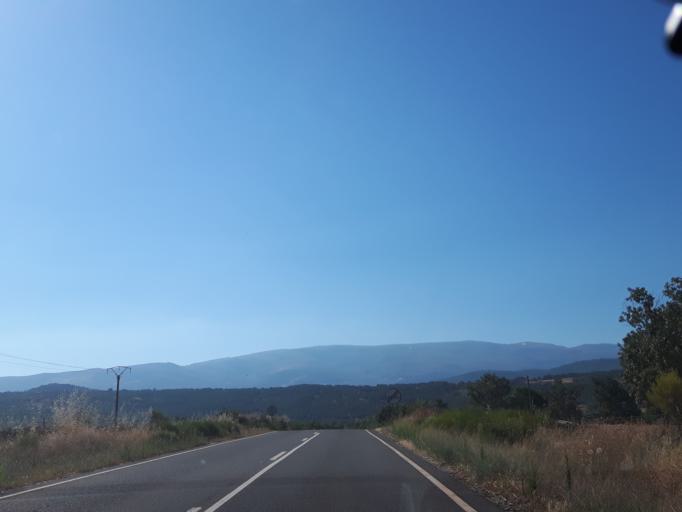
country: ES
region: Castille and Leon
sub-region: Provincia de Salamanca
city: Valdehijaderos
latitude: 40.4283
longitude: -5.8198
